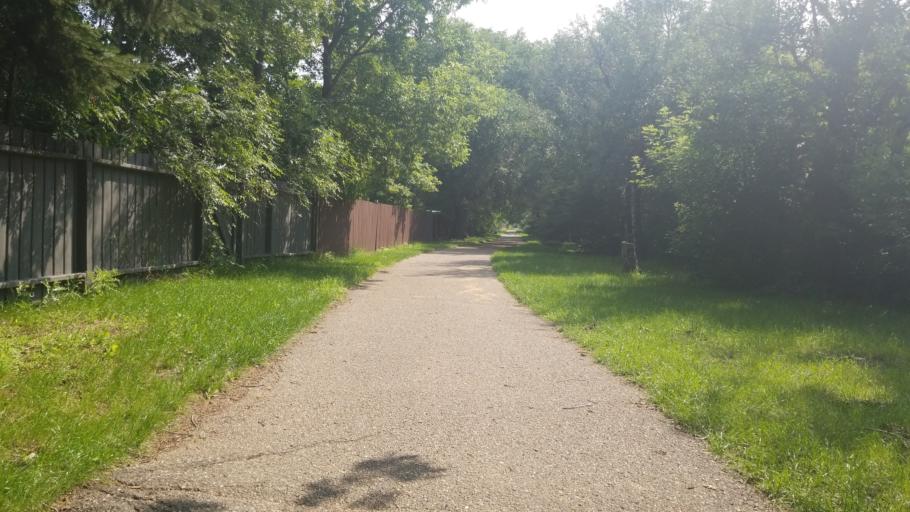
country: CA
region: Saskatchewan
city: Lloydminster
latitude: 53.2681
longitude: -110.0176
